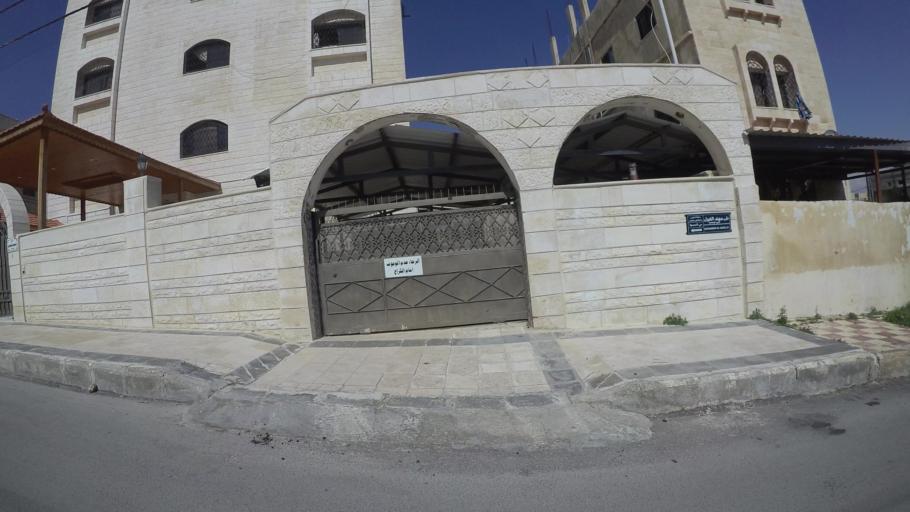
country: JO
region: Amman
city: Al Bunayyat ash Shamaliyah
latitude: 31.9026
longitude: 35.8996
